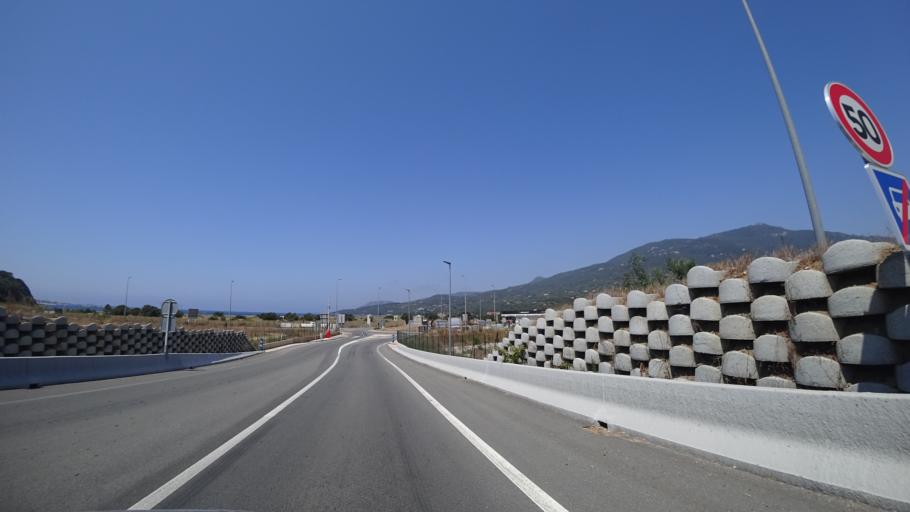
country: FR
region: Corsica
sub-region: Departement de la Corse-du-Sud
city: Propriano
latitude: 41.6838
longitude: 8.9223
